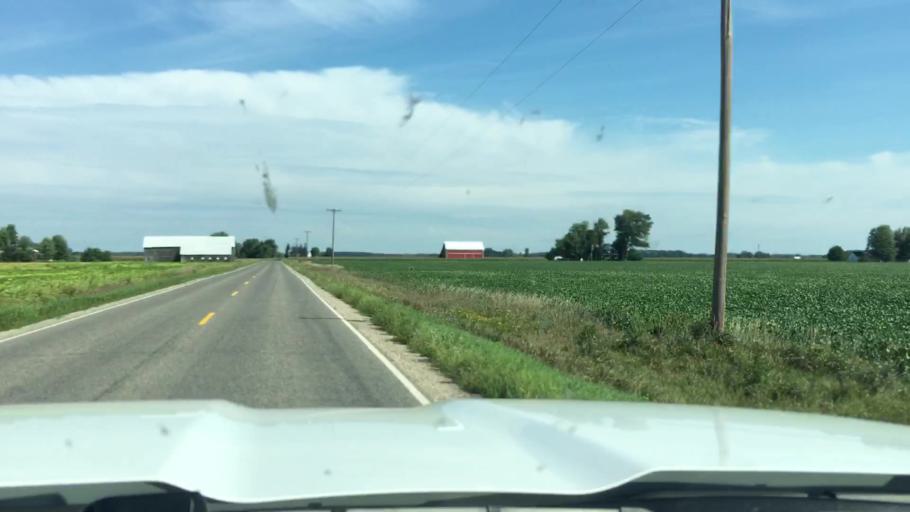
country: US
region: Michigan
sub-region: Saginaw County
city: Hemlock
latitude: 43.5069
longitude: -84.2297
